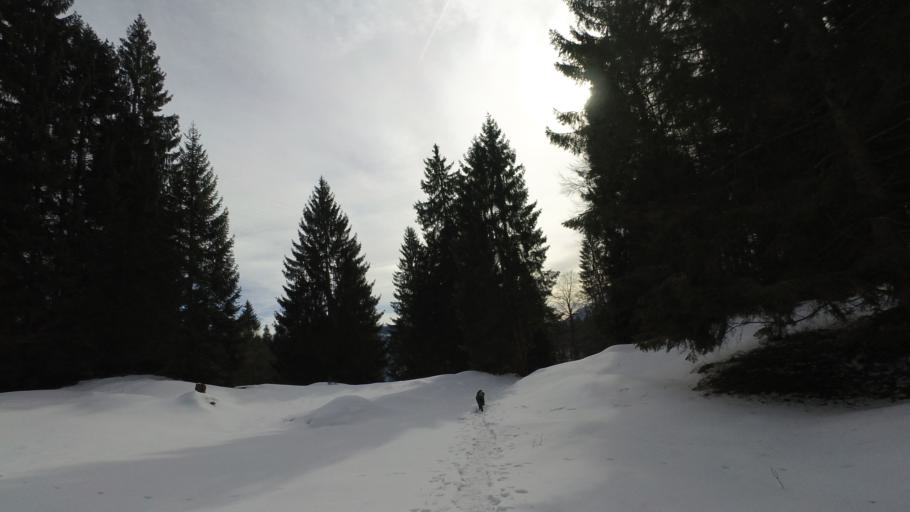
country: DE
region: Bavaria
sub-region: Upper Bavaria
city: Reit im Winkl
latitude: 47.6892
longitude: 12.4451
